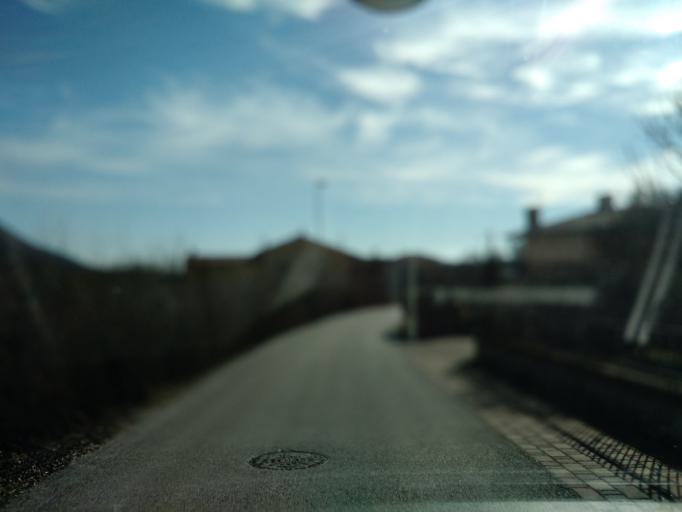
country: IT
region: Veneto
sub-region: Provincia di Vicenza
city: Cogollo del Cengio
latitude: 45.7922
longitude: 11.4047
